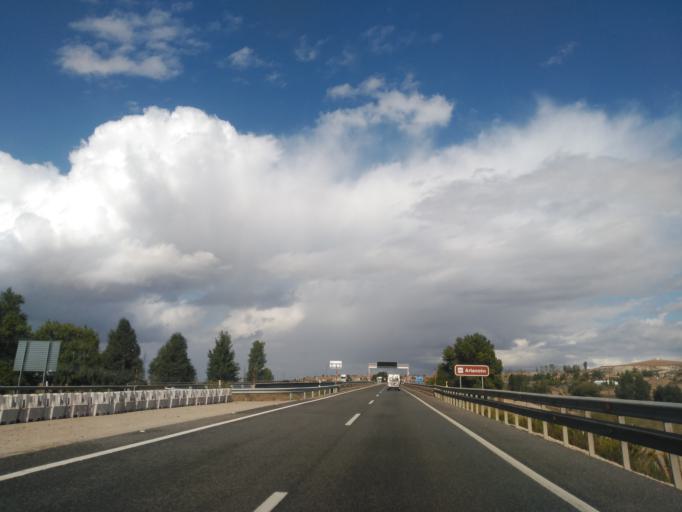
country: ES
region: Castille and Leon
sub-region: Provincia de Burgos
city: Frandovinez
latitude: 42.3002
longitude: -3.8348
